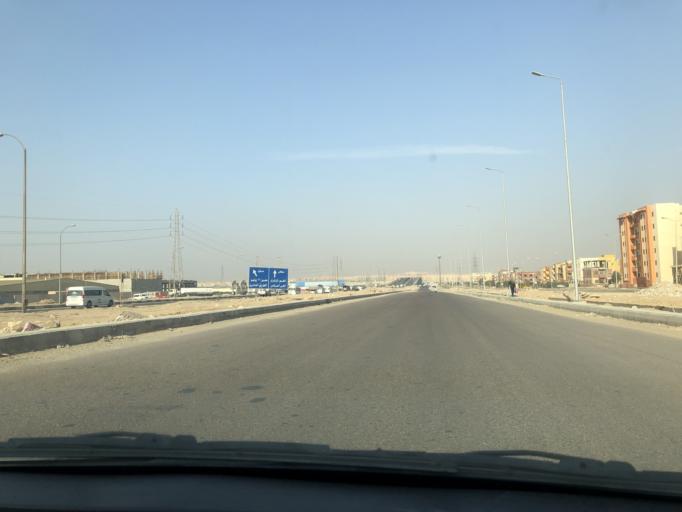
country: EG
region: Al Jizah
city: Madinat Sittah Uktubar
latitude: 29.9055
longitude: 30.9197
